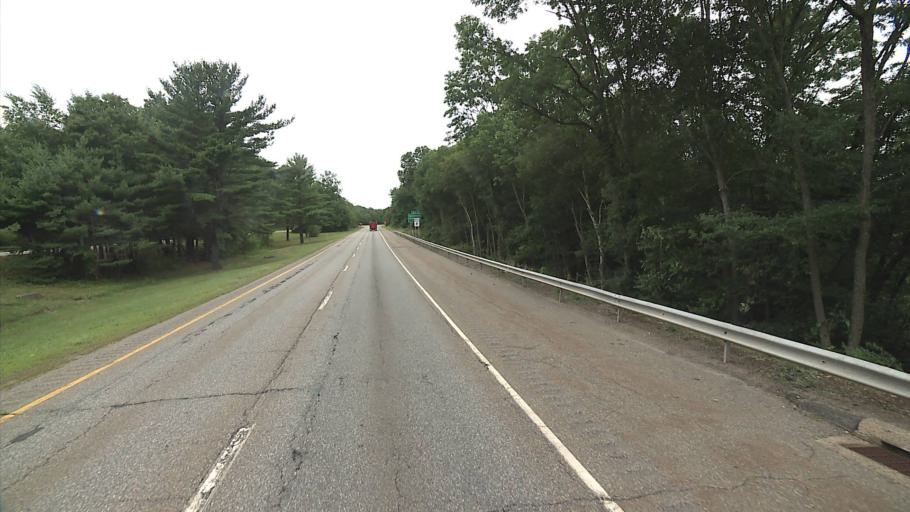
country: US
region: Connecticut
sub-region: Litchfield County
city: Thomaston
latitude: 41.7124
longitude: -73.0876
